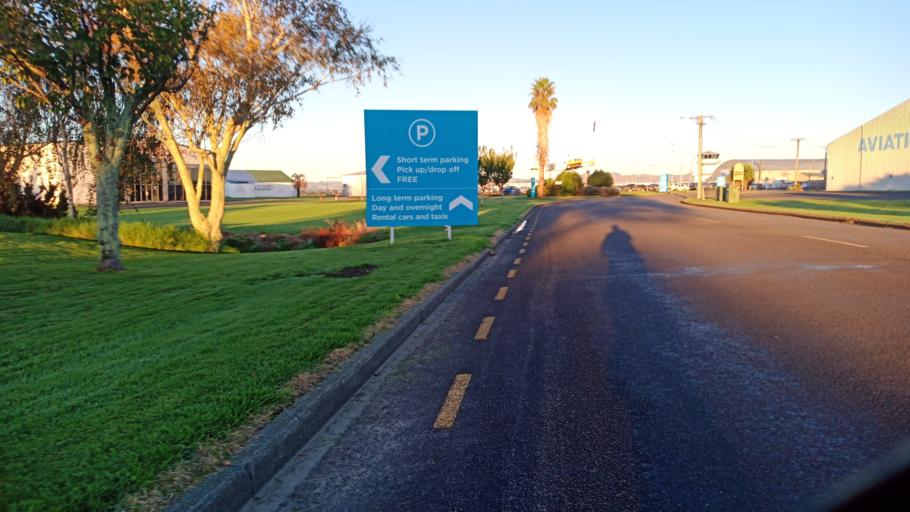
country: NZ
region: Gisborne
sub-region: Gisborne District
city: Gisborne
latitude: -38.6613
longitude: 177.9850
